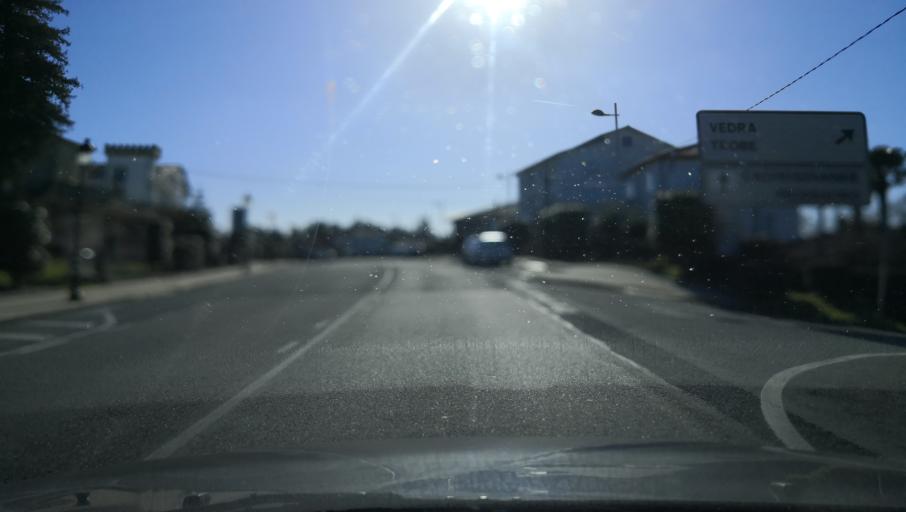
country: ES
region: Galicia
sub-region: Provincia da Coruna
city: Vedra
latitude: 42.7966
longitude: -8.4685
